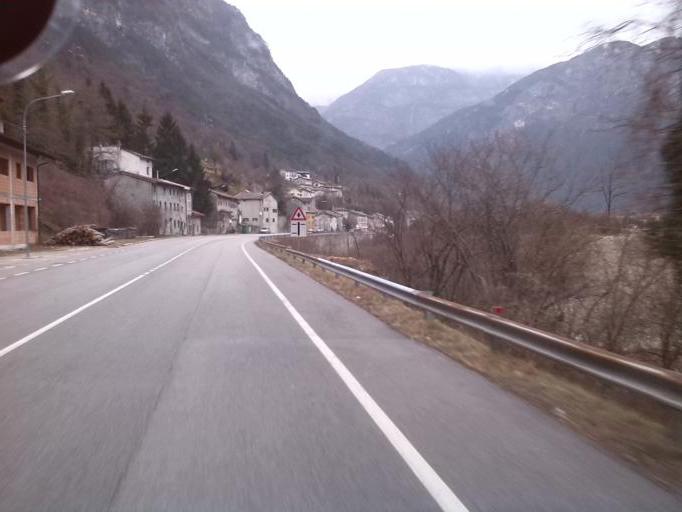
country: IT
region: Friuli Venezia Giulia
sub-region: Provincia di Udine
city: Chiusaforte
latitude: 46.4031
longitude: 13.2895
